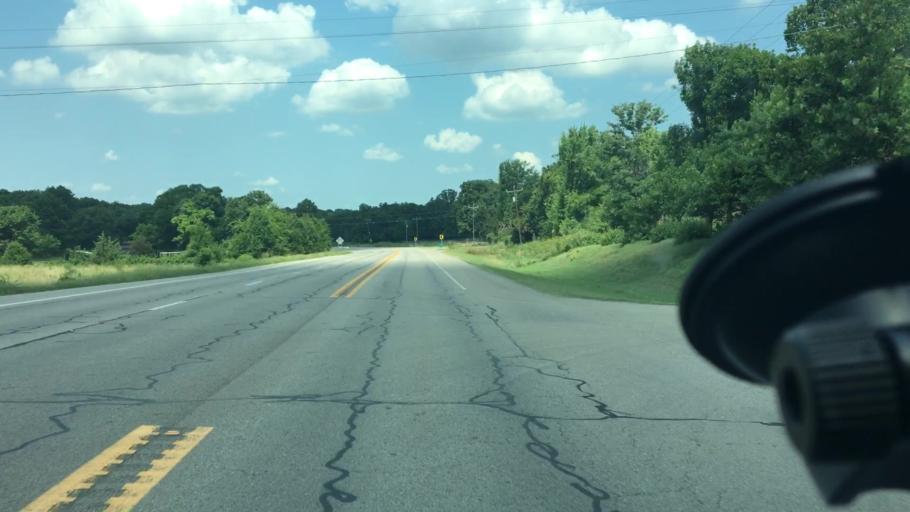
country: US
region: Arkansas
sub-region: Logan County
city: Paris
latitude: 35.2992
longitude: -93.8289
